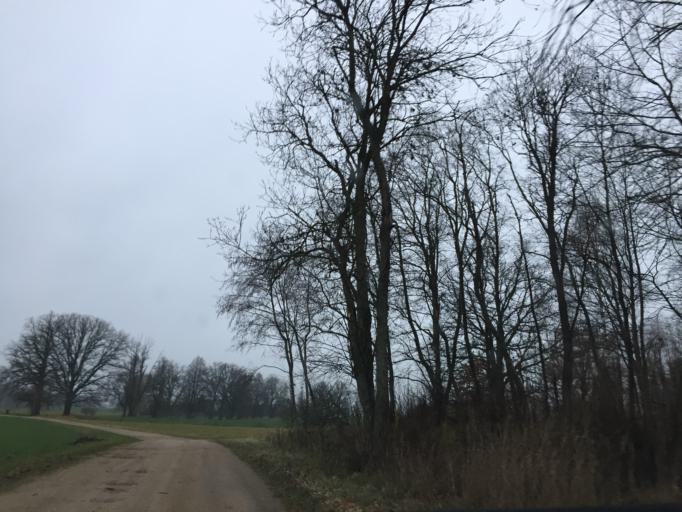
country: LV
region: Koceni
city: Koceni
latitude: 57.5513
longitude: 25.3569
